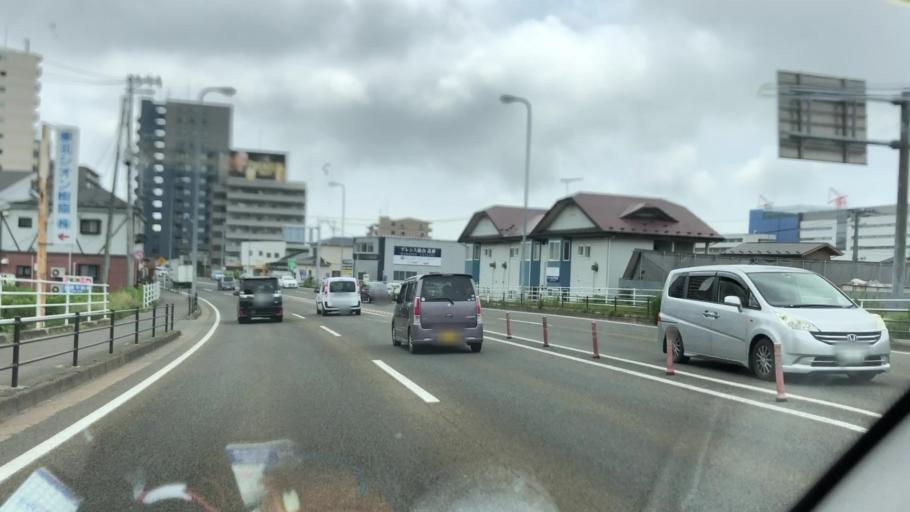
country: JP
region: Miyagi
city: Rifu
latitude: 38.2713
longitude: 140.9629
